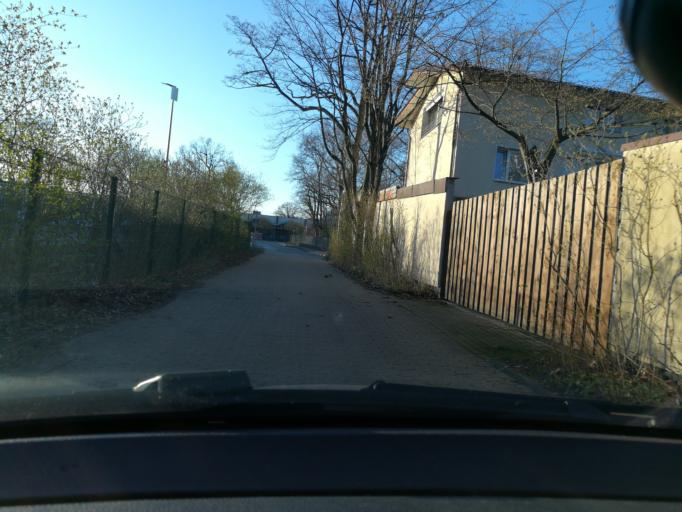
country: DE
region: North Rhine-Westphalia
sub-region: Regierungsbezirk Detmold
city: Oerlinghausen
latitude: 51.9558
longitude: 8.5832
